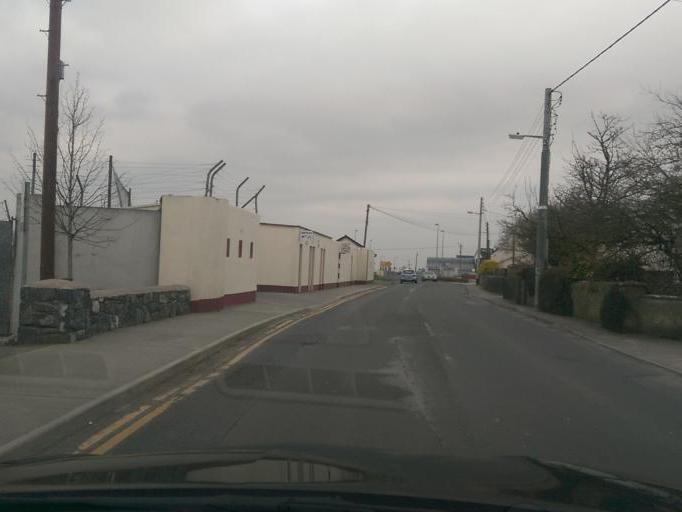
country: IE
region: Connaught
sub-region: County Galway
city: Athenry
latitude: 53.2968
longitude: -8.7506
